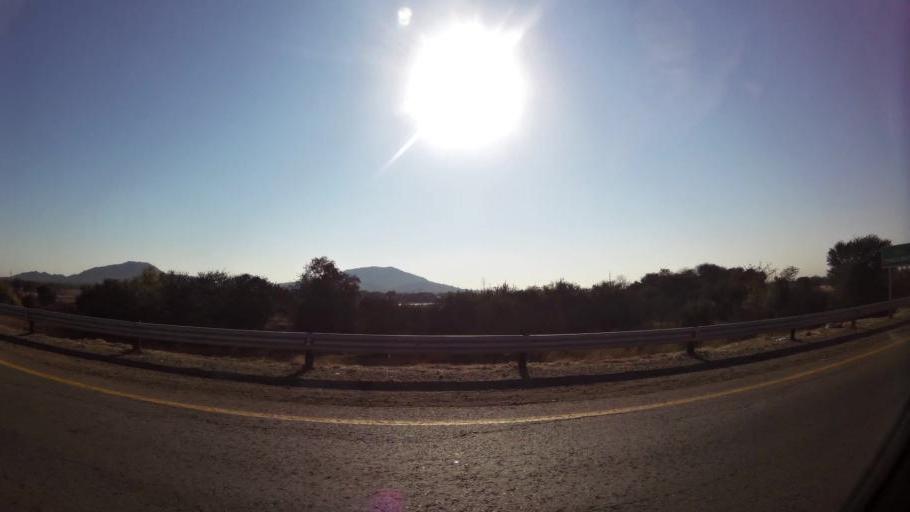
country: ZA
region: Gauteng
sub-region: City of Tshwane Metropolitan Municipality
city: Pretoria
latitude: -25.6484
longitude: 28.1545
